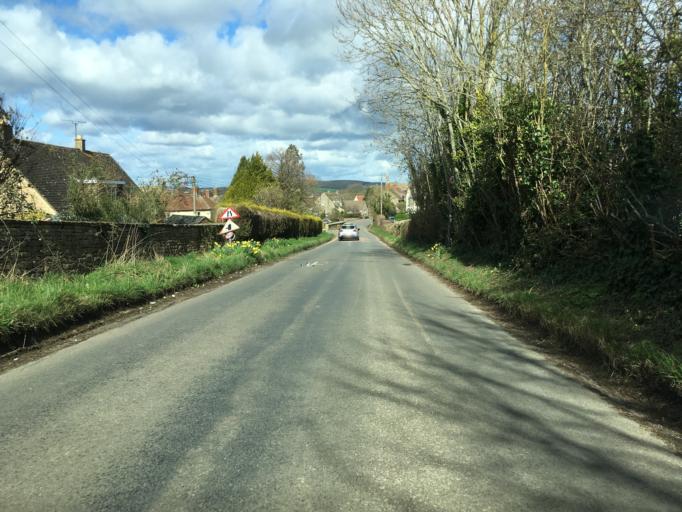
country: GB
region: England
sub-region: Gloucestershire
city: Wotton-under-Edge
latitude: 51.6027
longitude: -2.3347
